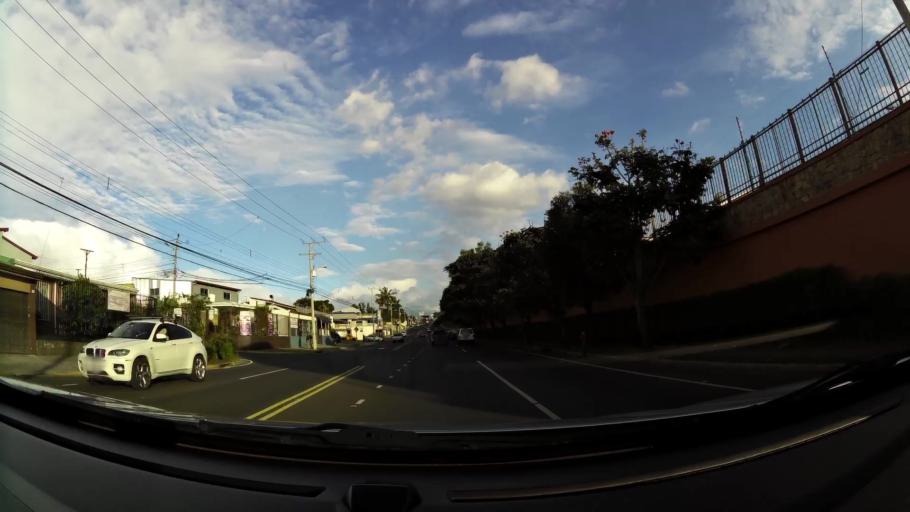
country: CR
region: Heredia
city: San Francisco
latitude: 9.9971
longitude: -84.1381
